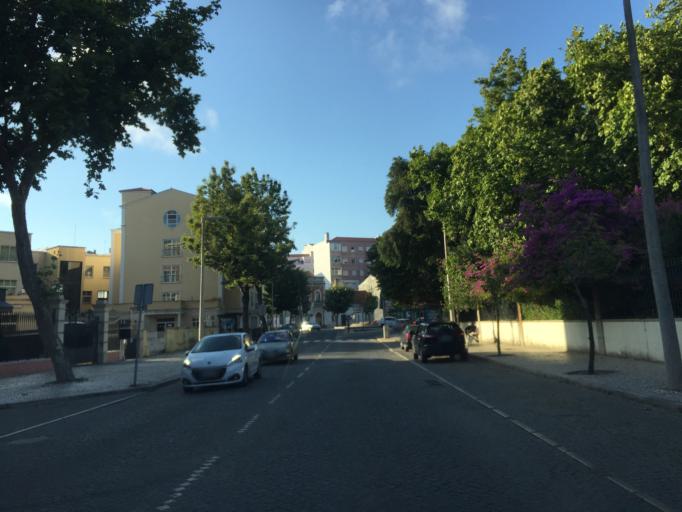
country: PT
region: Leiria
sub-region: Caldas da Rainha
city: Caldas da Rainha
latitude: 39.4013
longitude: -9.1360
